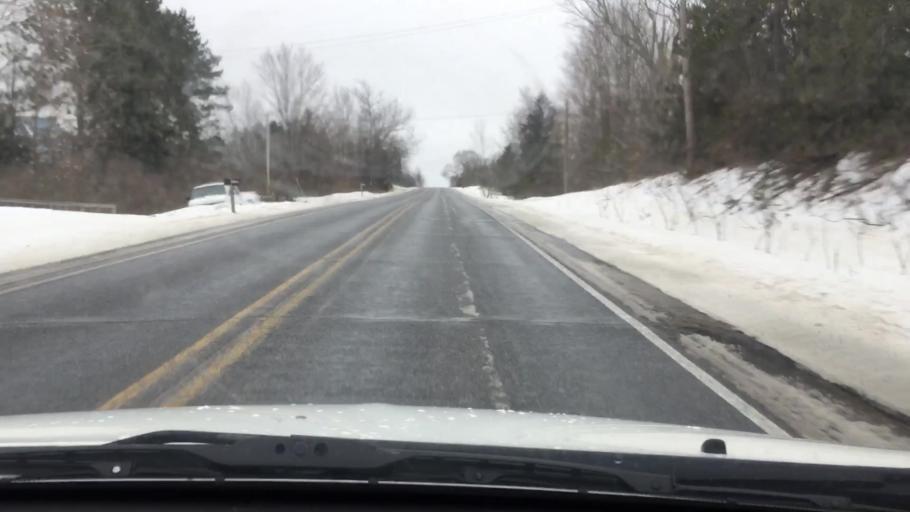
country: US
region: Michigan
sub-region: Wexford County
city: Cadillac
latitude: 44.0952
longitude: -85.4442
